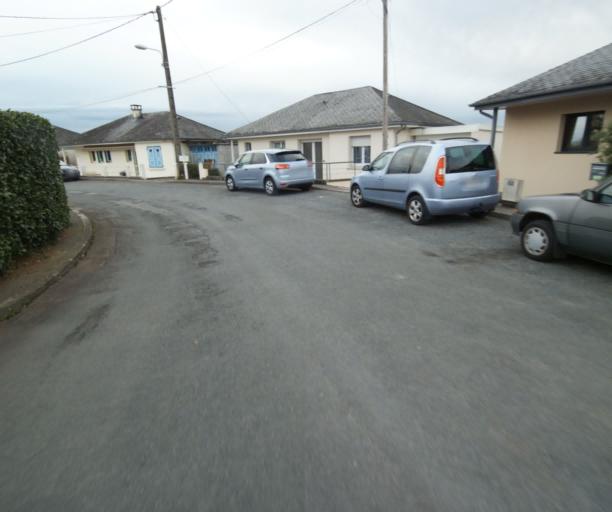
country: FR
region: Limousin
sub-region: Departement de la Correze
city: Tulle
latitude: 45.2600
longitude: 1.7612
